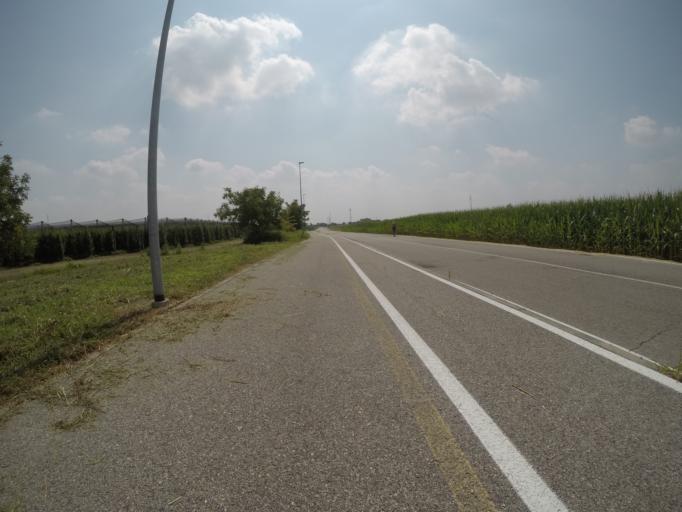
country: IT
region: Veneto
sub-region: Provincia di Rovigo
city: Villanova del Ghebbo Canton
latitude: 45.0567
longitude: 11.6471
